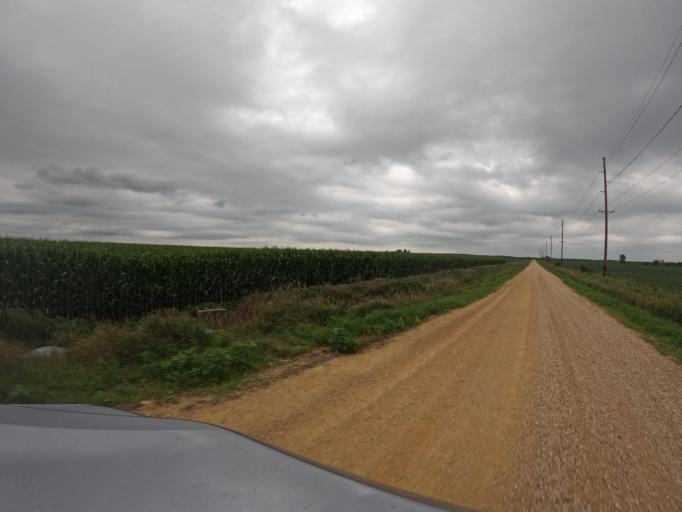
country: US
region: Iowa
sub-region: Clinton County
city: De Witt
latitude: 41.9382
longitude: -90.5948
